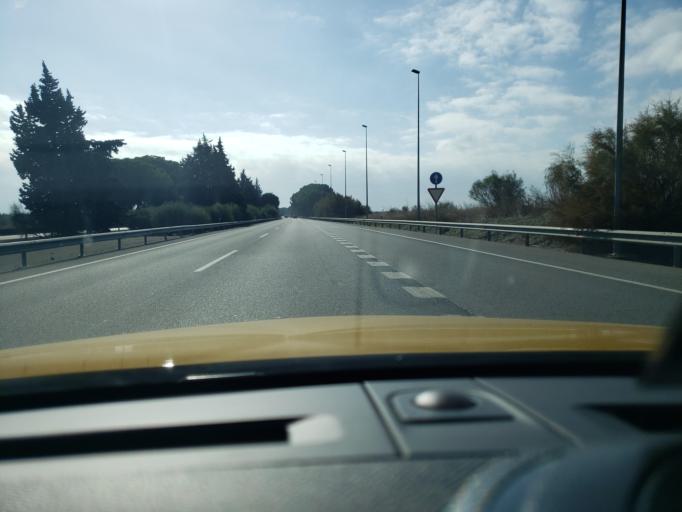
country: ES
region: Andalusia
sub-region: Provincia de Sevilla
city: Los Palacios y Villafranca
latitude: 37.1931
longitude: -5.9110
